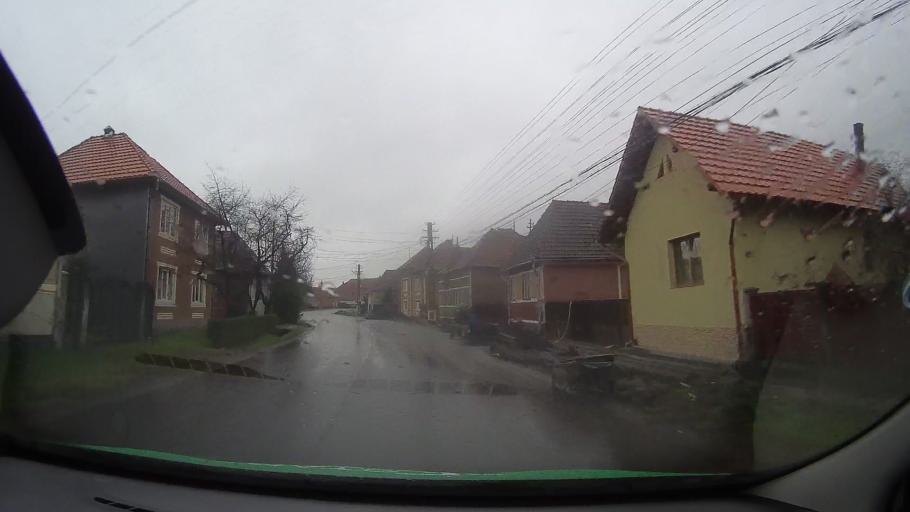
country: RO
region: Mures
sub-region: Comuna Alunis
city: Alunis
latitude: 46.8954
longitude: 24.8215
